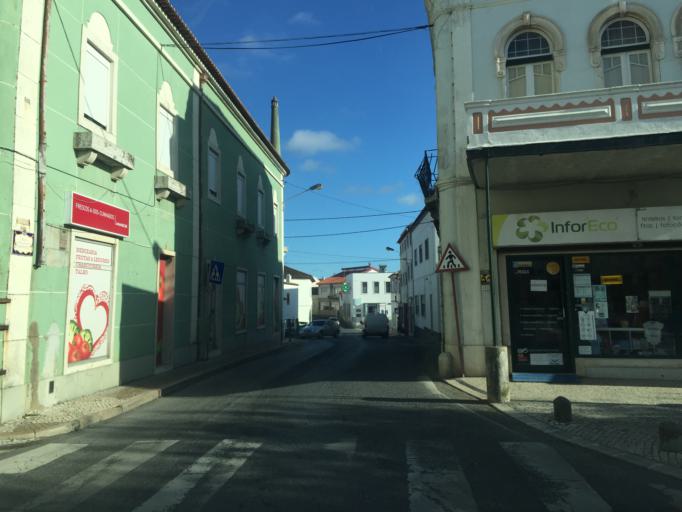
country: PT
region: Lisbon
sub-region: Torres Vedras
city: A dos Cunhados
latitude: 39.1517
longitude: -9.2983
